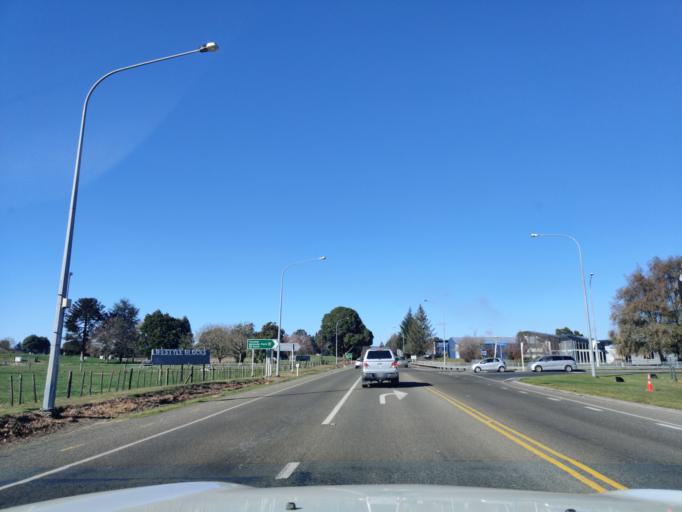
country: NZ
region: Waikato
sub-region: South Waikato District
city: Tokoroa
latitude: -38.2257
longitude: 175.8769
